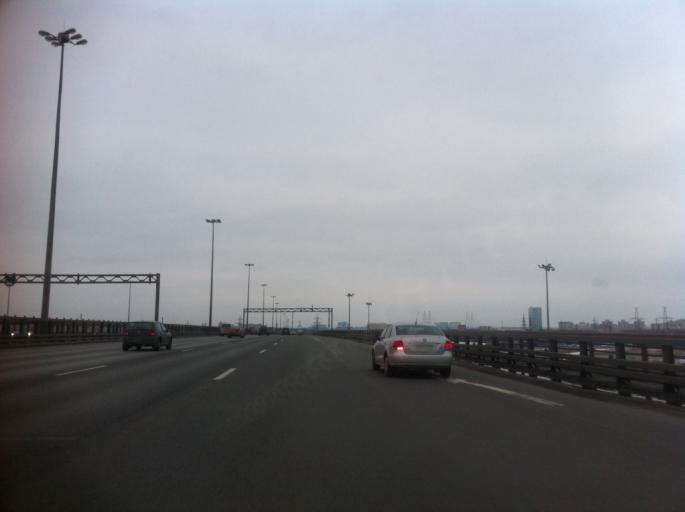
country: RU
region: St.-Petersburg
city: Obukhovo
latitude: 59.8298
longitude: 30.4416
